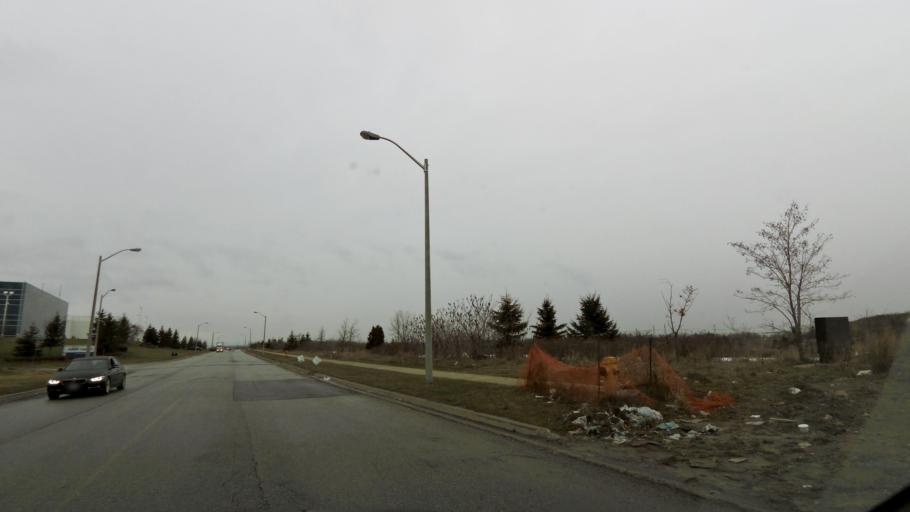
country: CA
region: Ontario
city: Etobicoke
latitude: 43.7776
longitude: -79.6395
